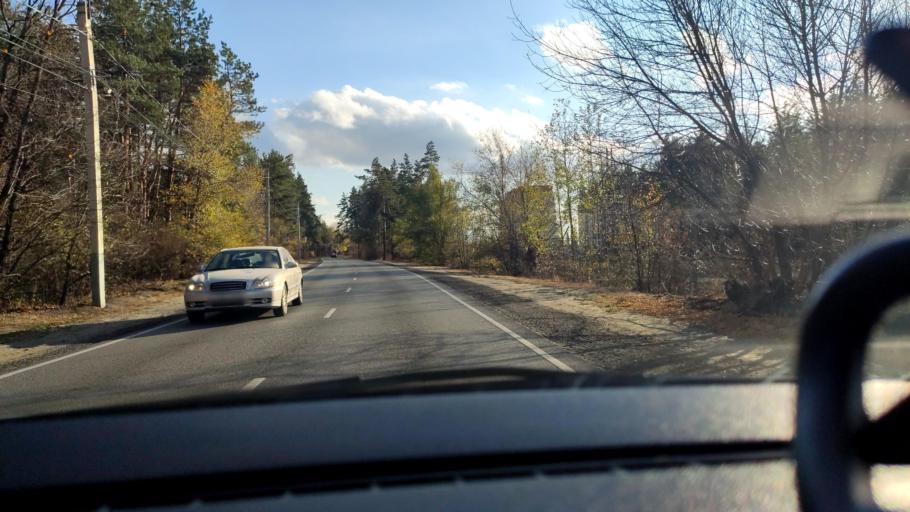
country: RU
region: Voronezj
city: Pridonskoy
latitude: 51.6286
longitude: 39.0818
